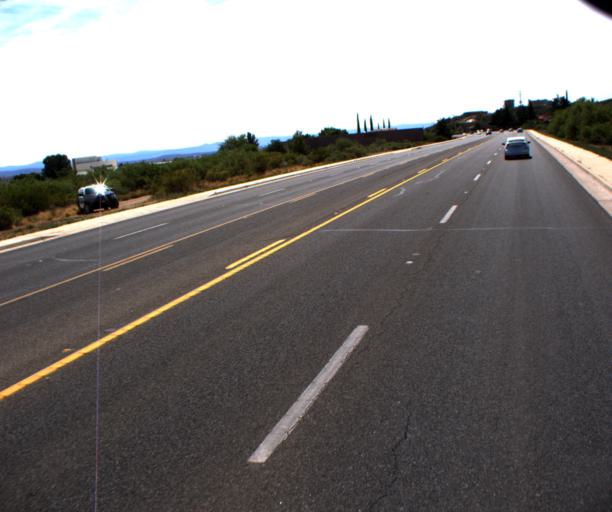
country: US
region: Arizona
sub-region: Yavapai County
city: Cottonwood
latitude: 34.7364
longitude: -112.0337
